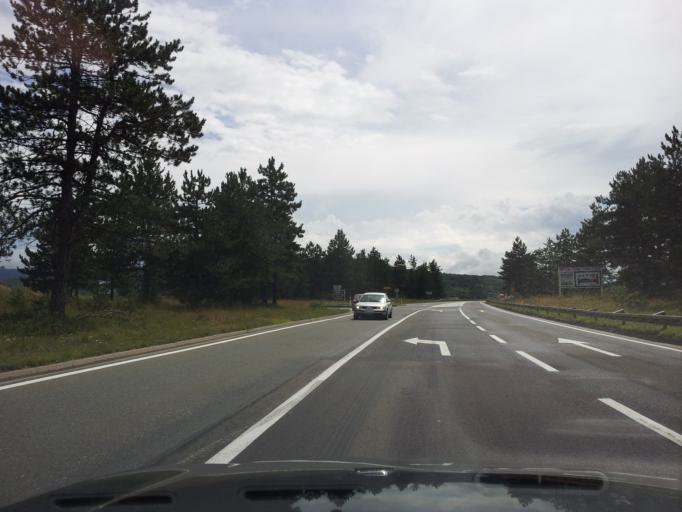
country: HR
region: Zadarska
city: Gracac
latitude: 44.5528
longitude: 15.7612
